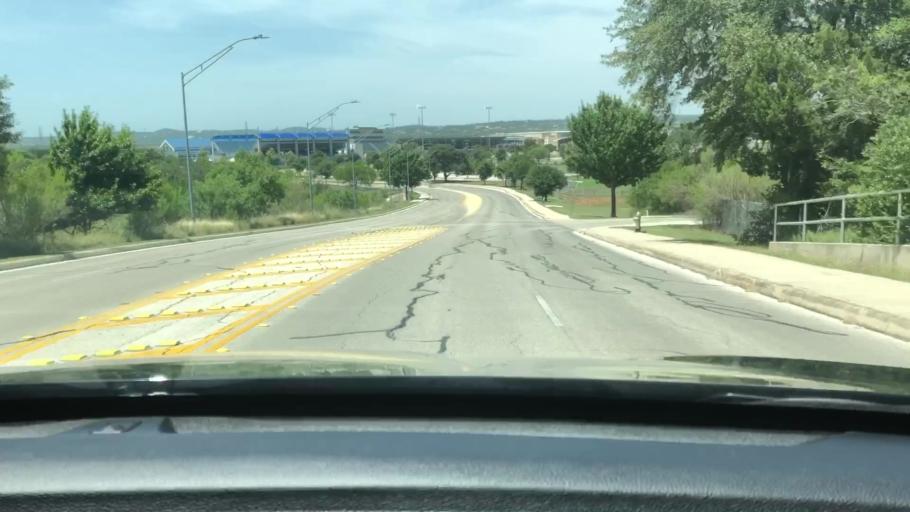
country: US
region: Texas
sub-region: Bexar County
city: Helotes
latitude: 29.5604
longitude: -98.6478
